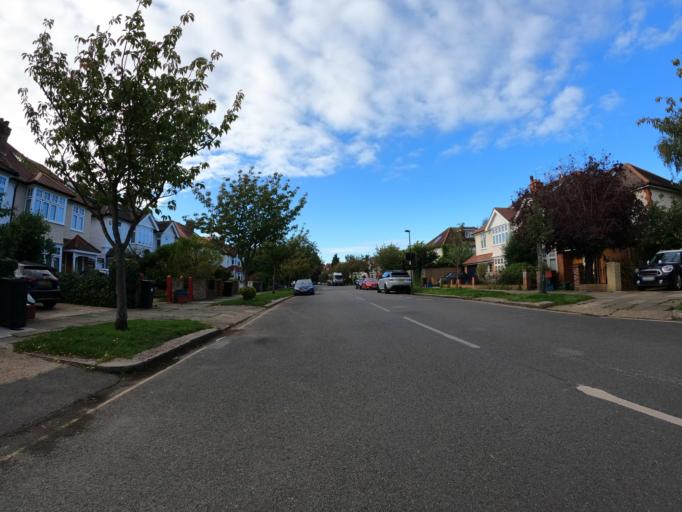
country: GB
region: England
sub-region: Greater London
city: Acton
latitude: 51.4840
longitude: -0.2672
